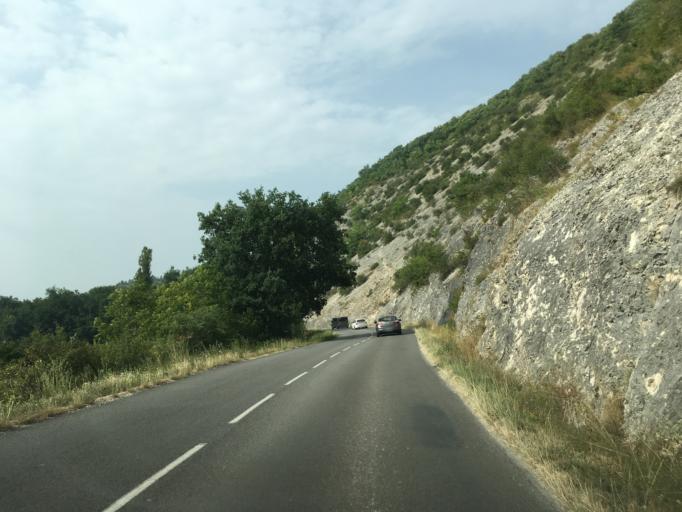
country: FR
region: Midi-Pyrenees
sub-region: Departement du Lot
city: Souillac
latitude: 44.8675
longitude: 1.4986
